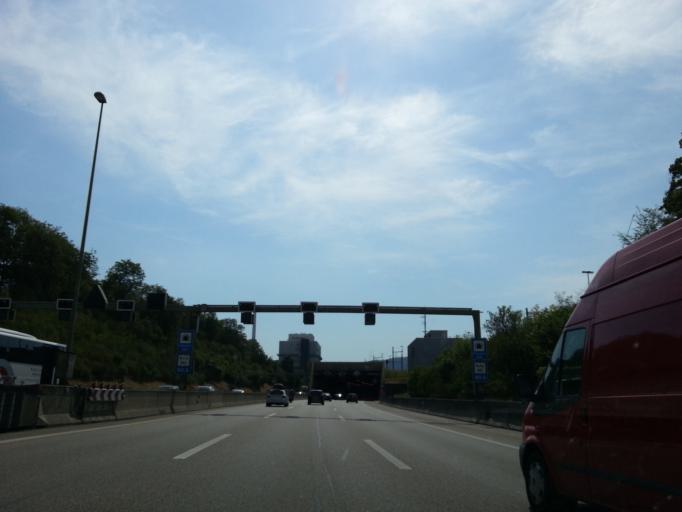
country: CH
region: Basel-Landschaft
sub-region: Bezirk Arlesheim
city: Muttenz
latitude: 47.5353
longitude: 7.6564
